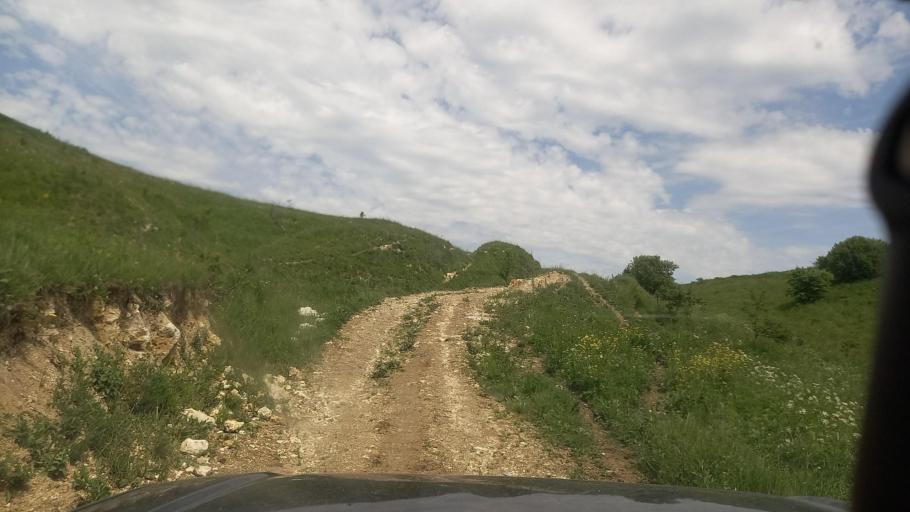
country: RU
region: Karachayevo-Cherkesiya
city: Pregradnaya
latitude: 44.0758
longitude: 41.2792
